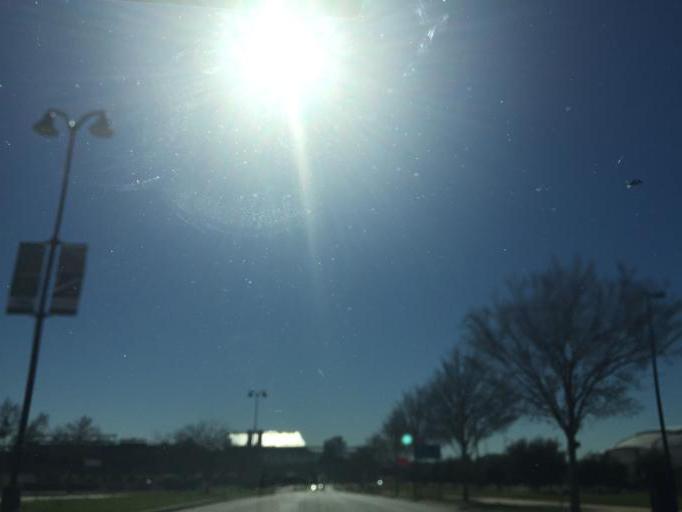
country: US
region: Texas
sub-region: Tarrant County
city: Arlington
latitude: 32.7591
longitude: -97.0854
